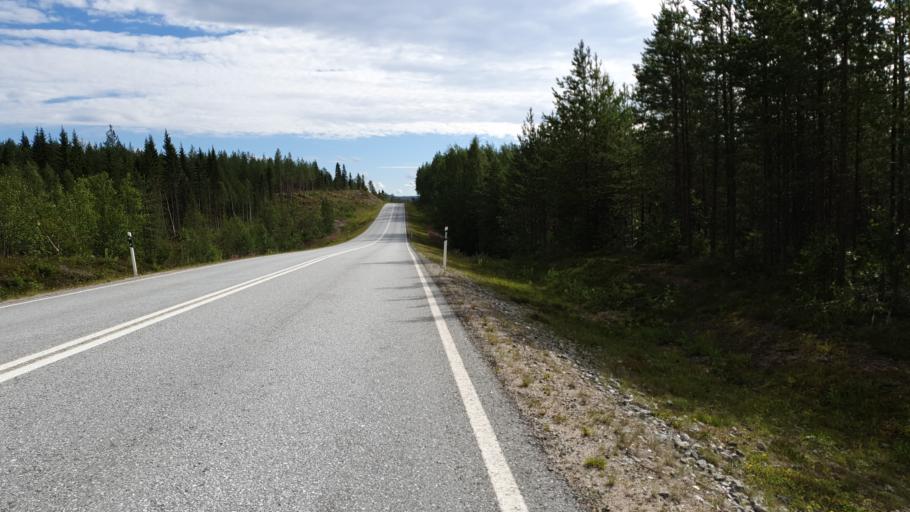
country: FI
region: Kainuu
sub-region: Kehys-Kainuu
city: Kuhmo
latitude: 64.4915
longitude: 29.8814
